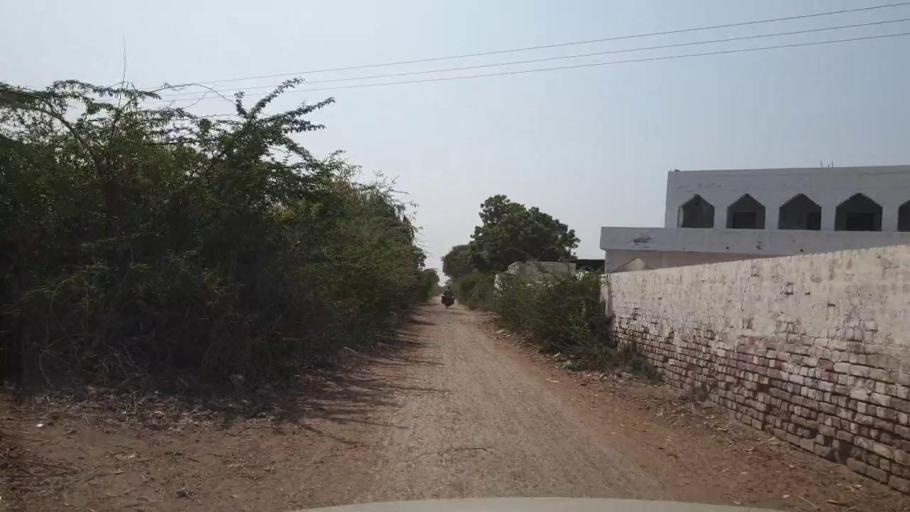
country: PK
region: Sindh
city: Dhoro Naro
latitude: 25.4629
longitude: 69.6315
